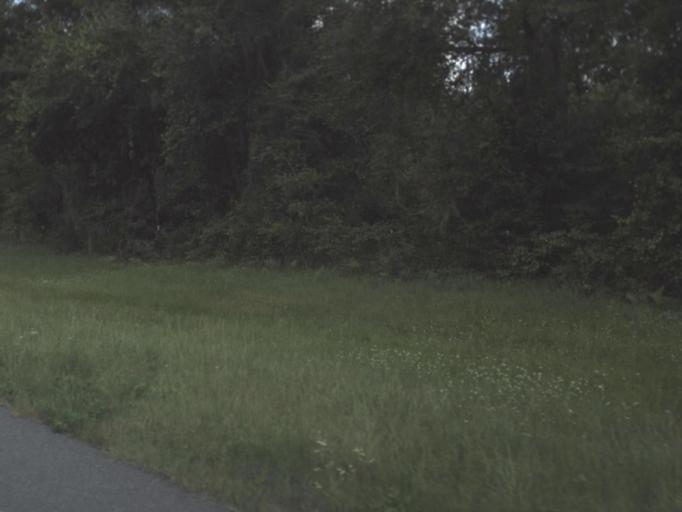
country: US
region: Florida
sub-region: Alachua County
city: Alachua
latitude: 29.8224
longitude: -82.4376
